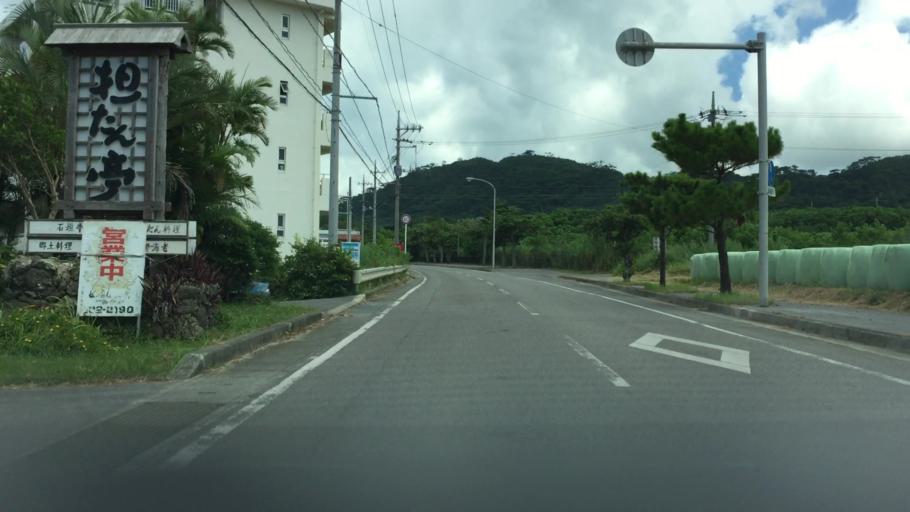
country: JP
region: Okinawa
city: Ishigaki
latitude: 24.3619
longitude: 124.1432
